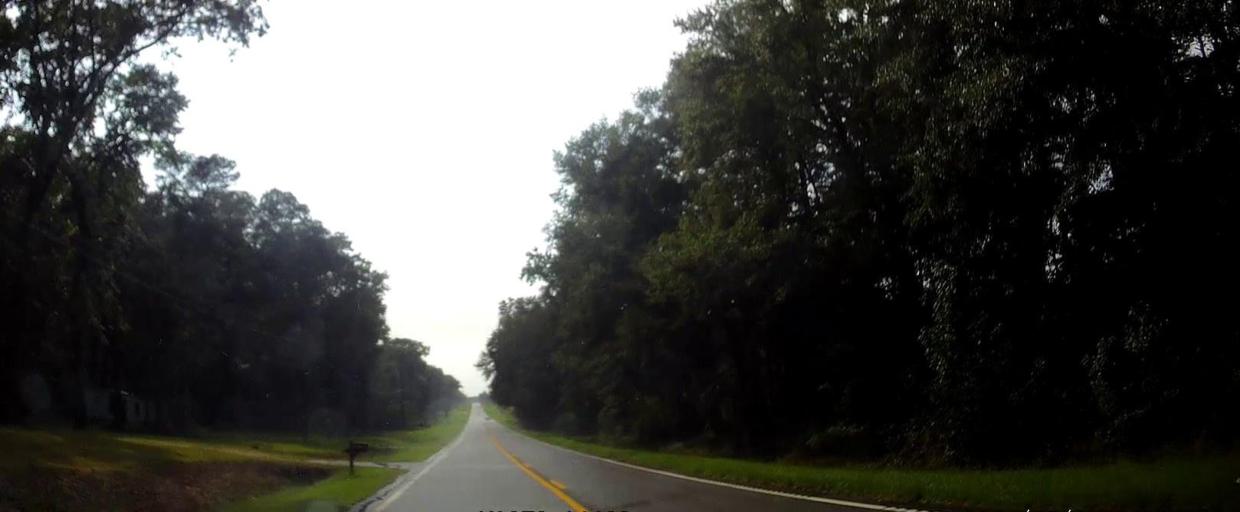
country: US
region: Georgia
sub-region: Twiggs County
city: Jeffersonville
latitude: 32.6052
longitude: -83.2550
